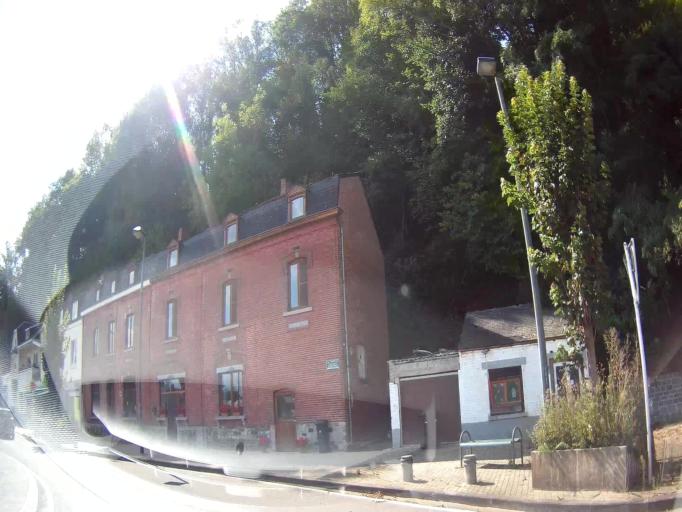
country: BE
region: Wallonia
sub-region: Province de Namur
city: Profondeville
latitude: 50.3492
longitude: 4.8517
